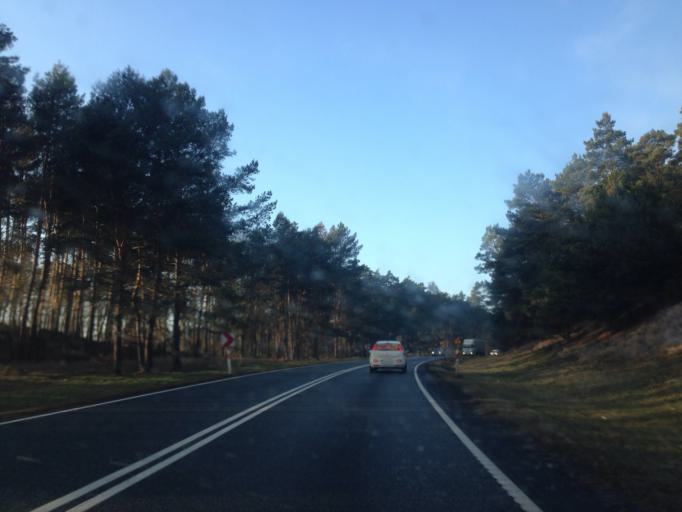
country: PL
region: Kujawsko-Pomorskie
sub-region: Powiat torunski
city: Wielka Nieszawka
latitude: 53.0008
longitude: 18.4526
